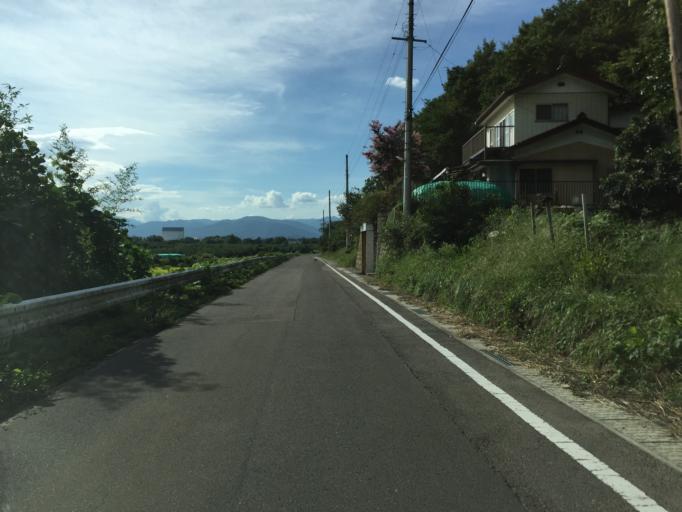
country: JP
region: Fukushima
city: Hobaramachi
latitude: 37.7997
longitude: 140.5138
